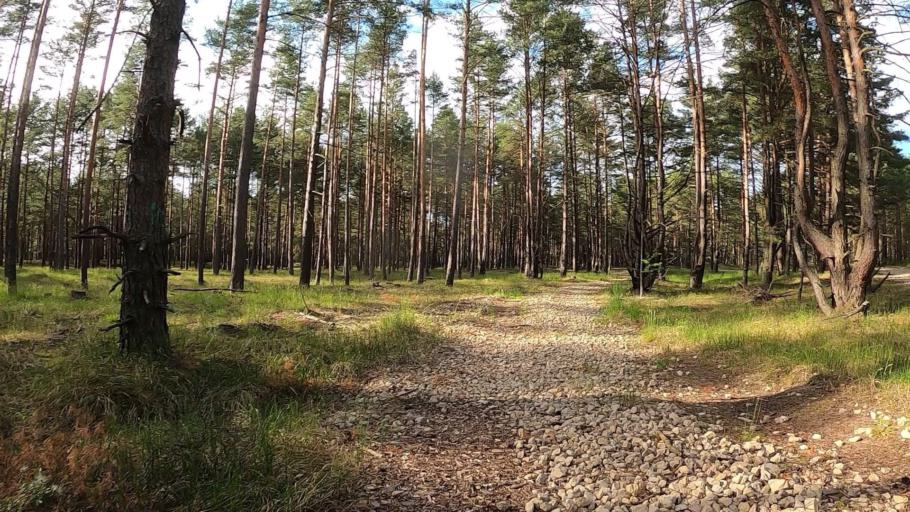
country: LV
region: Riga
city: Jaunciems
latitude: 57.0593
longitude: 24.1268
